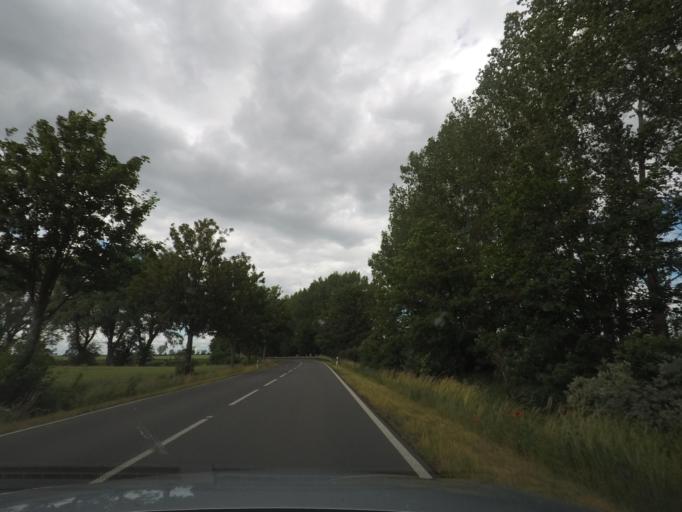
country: DE
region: Saxony-Anhalt
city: Ausleben
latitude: 52.0790
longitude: 11.0771
